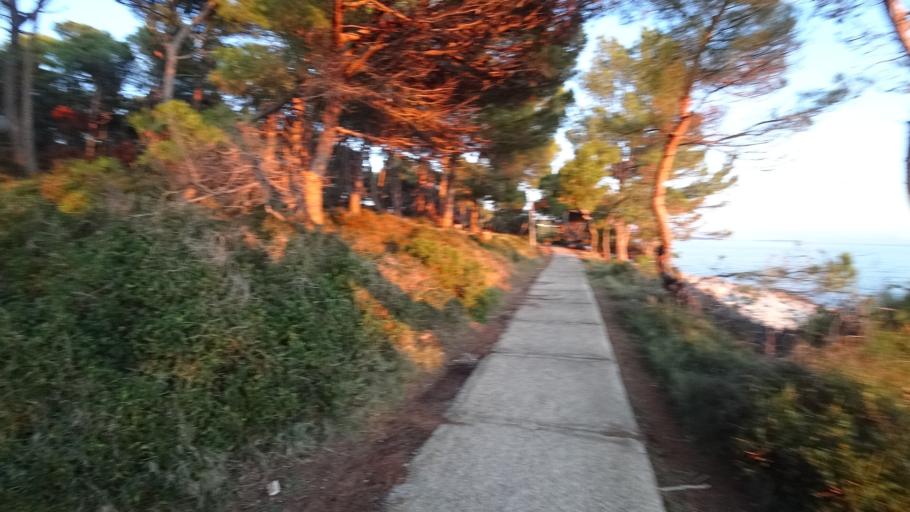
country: HR
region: Primorsko-Goranska
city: Mali Losinj
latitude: 44.5241
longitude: 14.4507
